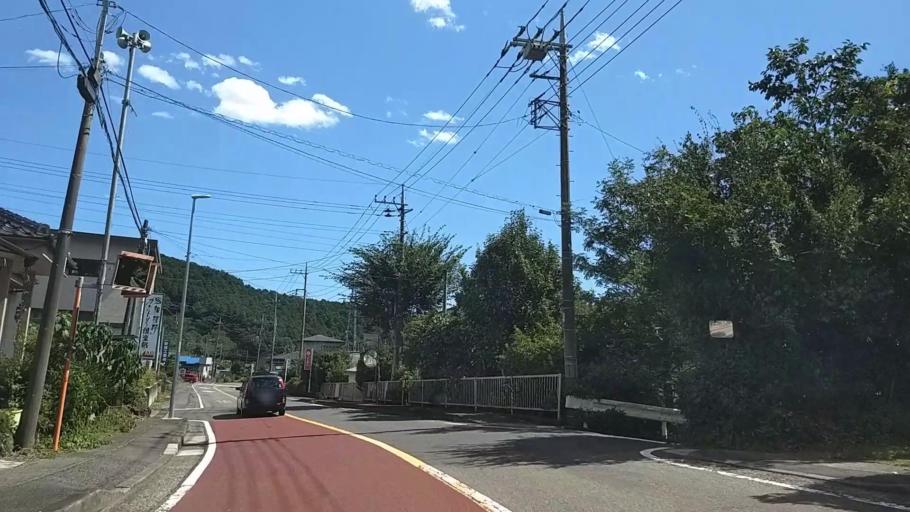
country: JP
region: Tokyo
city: Hachioji
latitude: 35.5489
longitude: 139.2953
